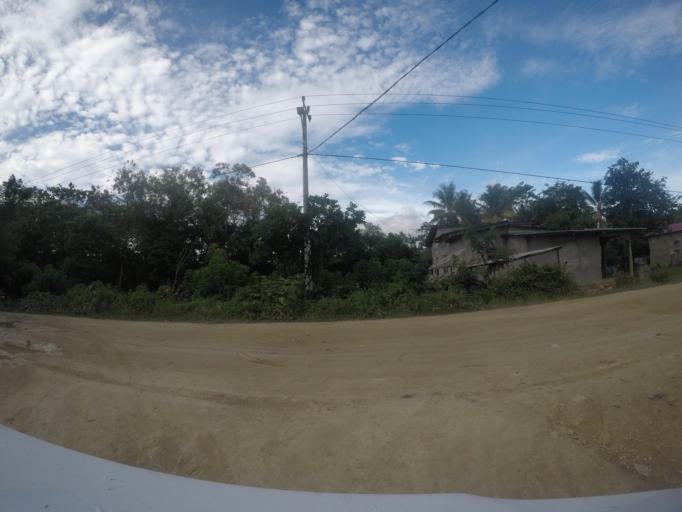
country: TL
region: Lautem
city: Lospalos
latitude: -8.4980
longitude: 126.9960
